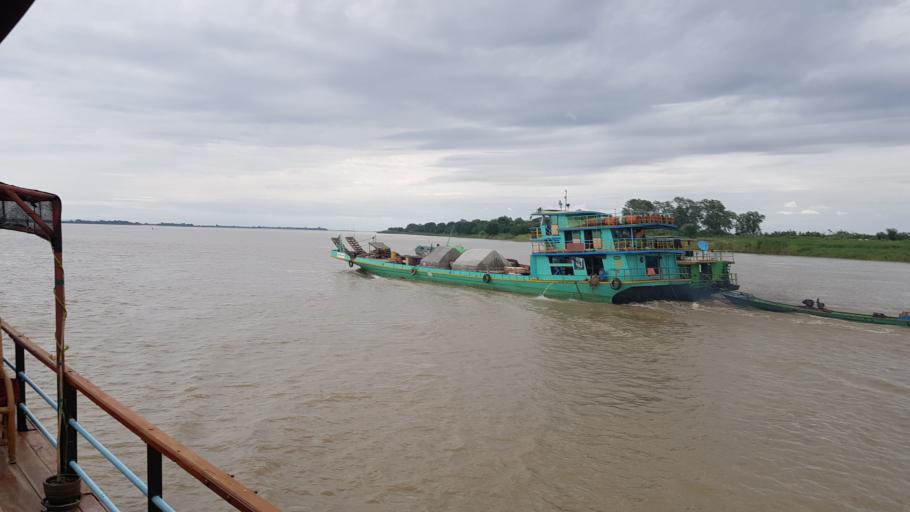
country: MM
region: Sagain
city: Sagaing
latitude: 21.9183
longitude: 95.5989
